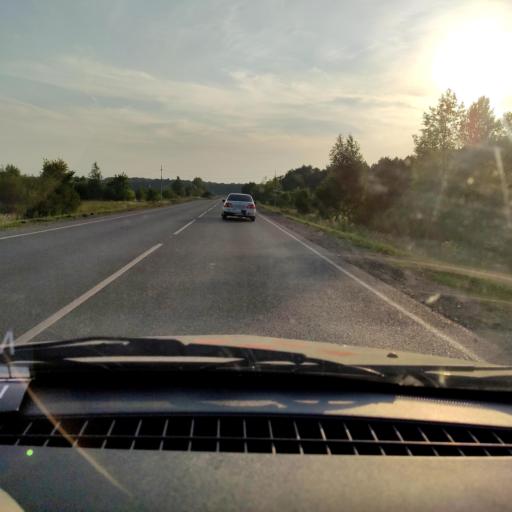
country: RU
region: Bashkortostan
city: Avdon
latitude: 54.5745
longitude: 55.7101
